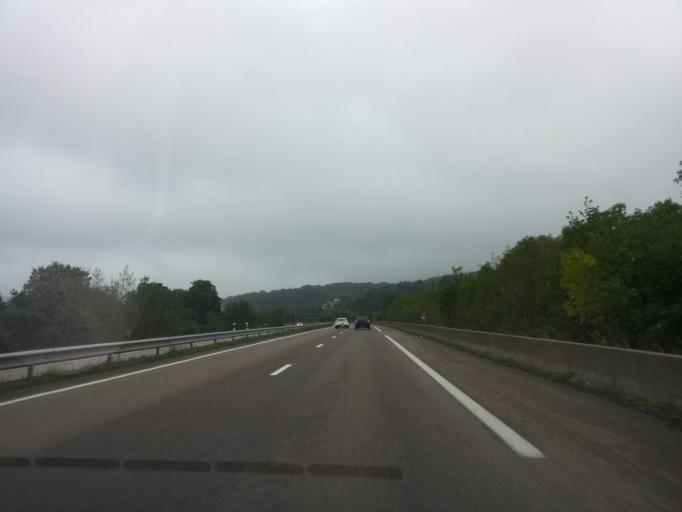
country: FR
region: Lorraine
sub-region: Departement des Vosges
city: Archettes
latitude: 48.1185
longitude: 6.5355
